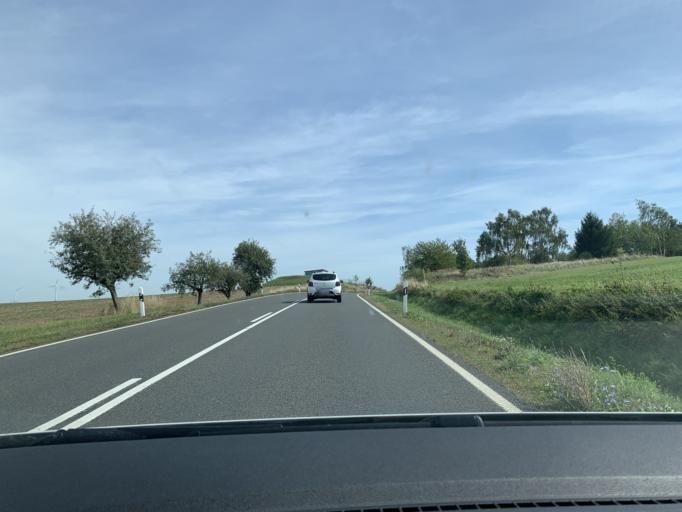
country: DE
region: Thuringia
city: Ronneburg
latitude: 50.8730
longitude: 12.1620
